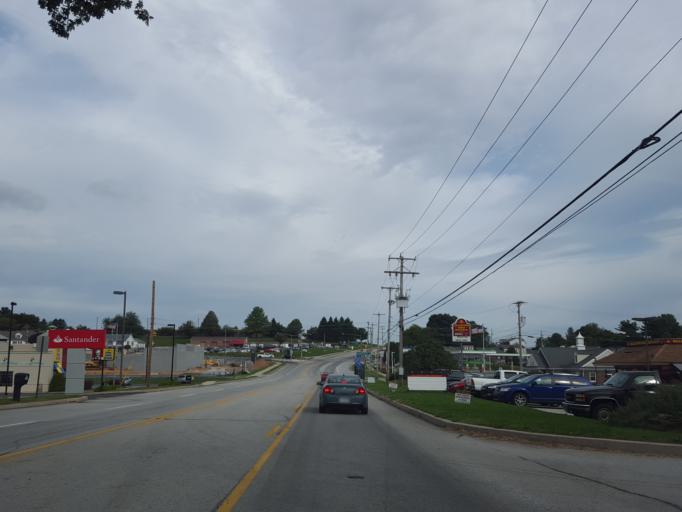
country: US
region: Pennsylvania
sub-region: York County
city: Spry
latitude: 39.9093
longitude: -76.6811
